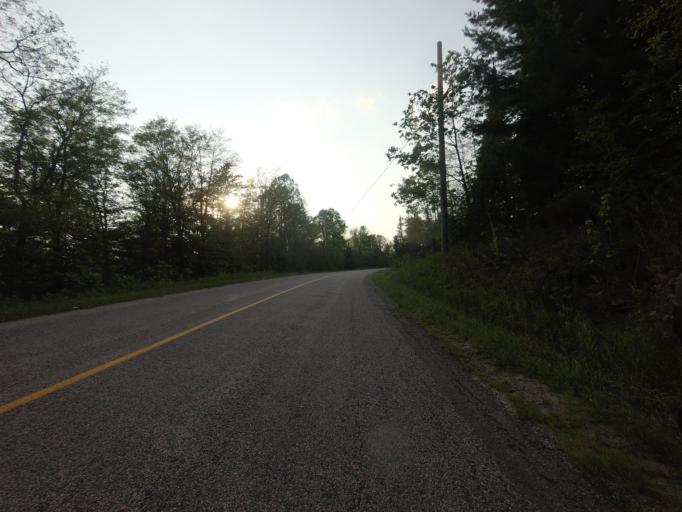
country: CA
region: Ontario
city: Renfrew
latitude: 44.9935
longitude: -76.7448
